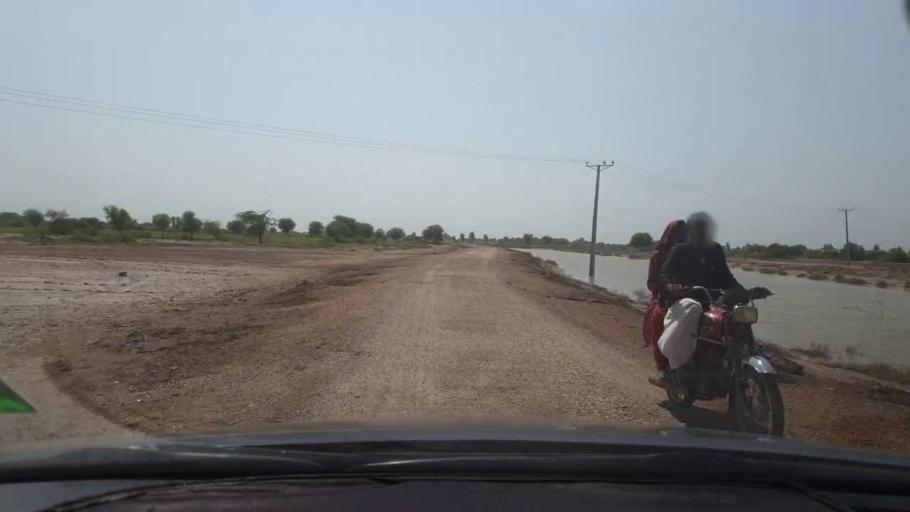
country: PK
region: Sindh
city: Tando Bago
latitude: 24.8161
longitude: 69.1650
